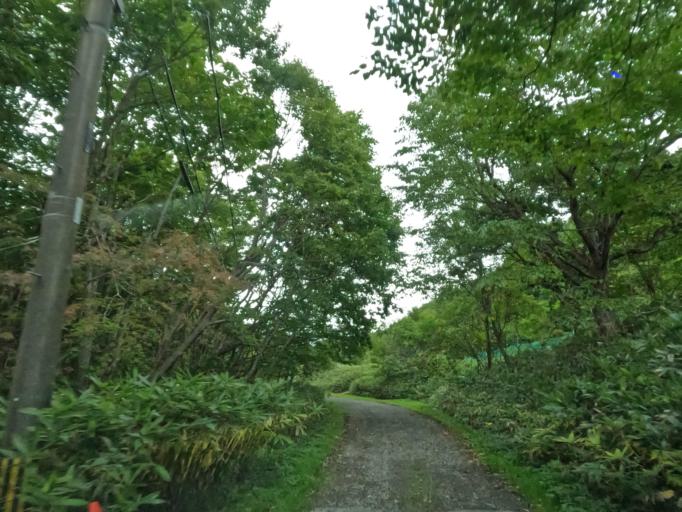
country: JP
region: Hokkaido
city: Muroran
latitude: 42.3693
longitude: 140.9666
